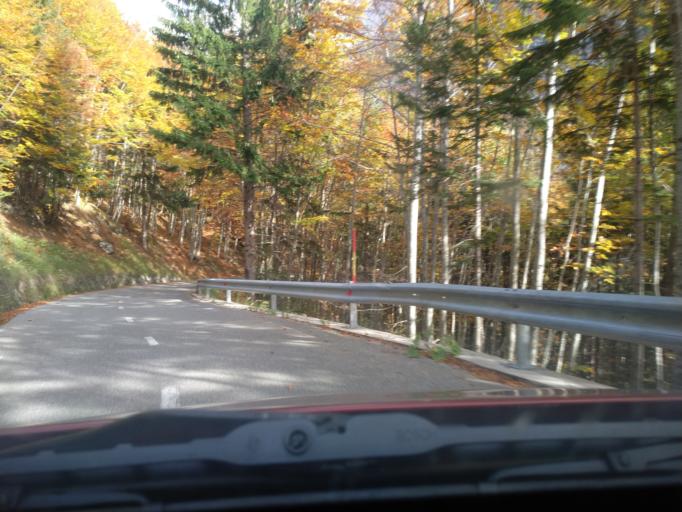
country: SI
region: Kranjska Gora
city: Kranjska Gora
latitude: 46.4076
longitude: 13.7528
